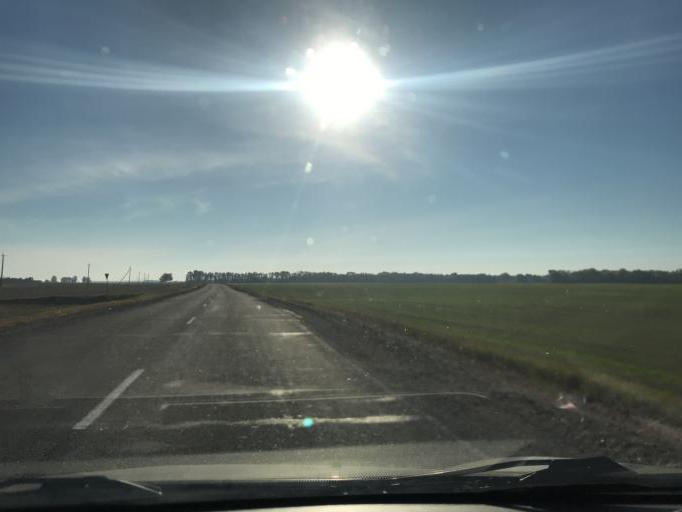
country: BY
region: Gomel
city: Brahin
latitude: 51.8034
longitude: 30.1212
